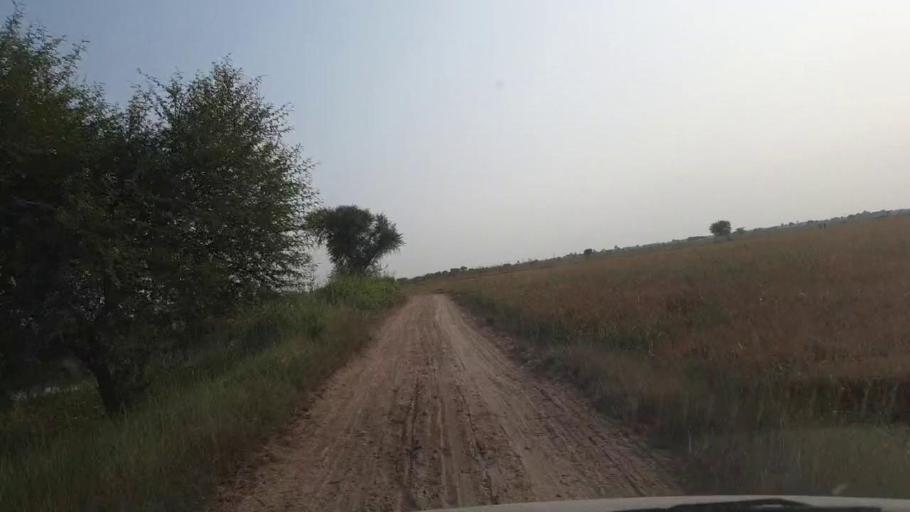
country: PK
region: Sindh
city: Matli
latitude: 25.0404
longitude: 68.7493
